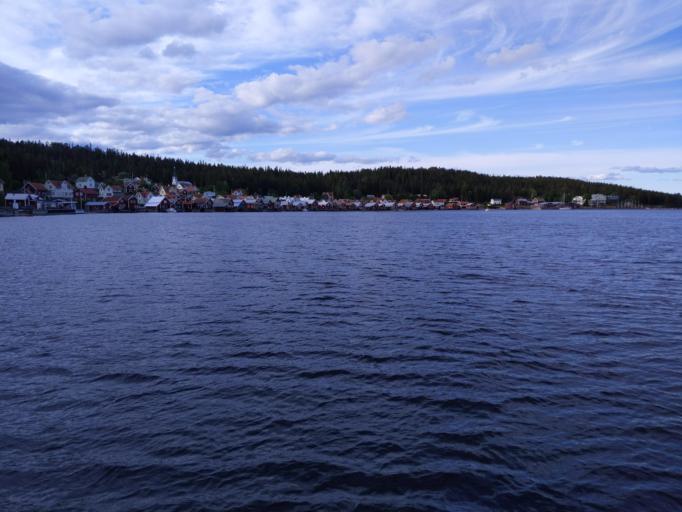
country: SE
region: Vaesternorrland
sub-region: OErnskoeldsviks Kommun
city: Kopmanholmen
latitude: 63.0182
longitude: 18.6467
